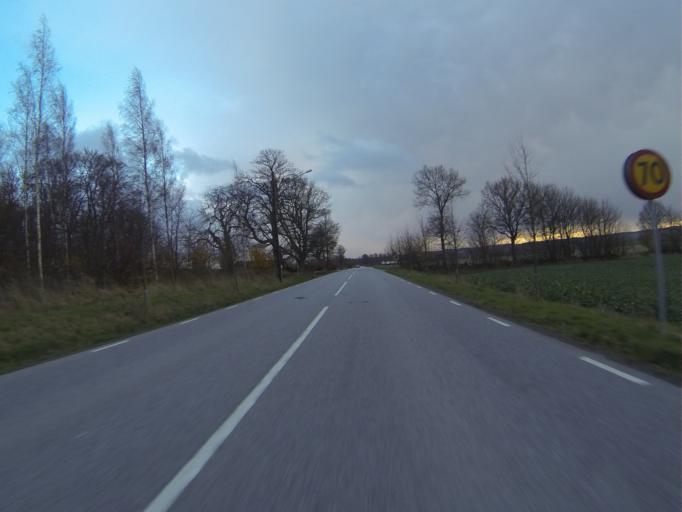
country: SE
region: Skane
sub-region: Lunds Kommun
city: Genarp
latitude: 55.6204
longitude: 13.4058
